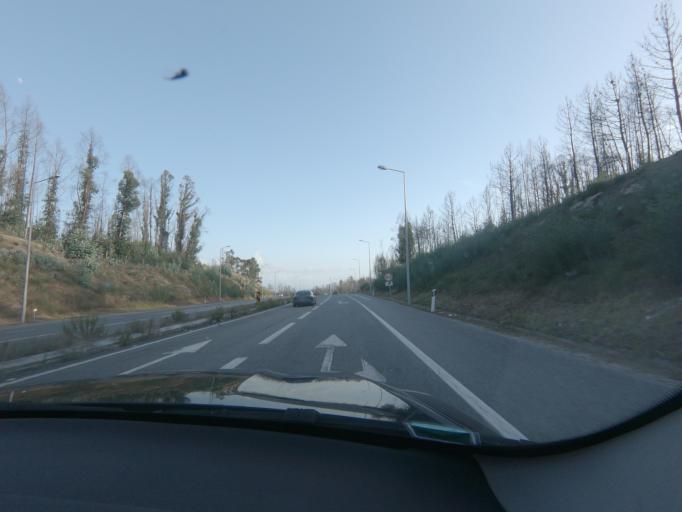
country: PT
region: Viseu
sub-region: Santa Comba Dao
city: Santa Comba Dao
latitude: 40.4405
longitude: -8.1088
